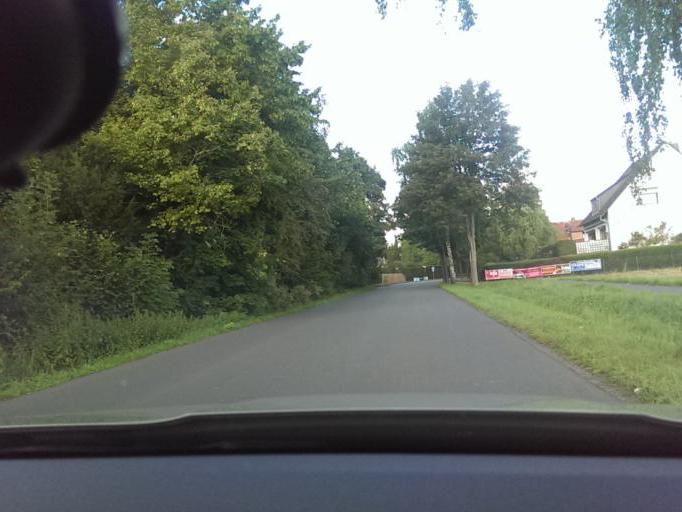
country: DE
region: Lower Saxony
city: Isernhagen Farster Bauerschaft
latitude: 52.4589
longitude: 9.8271
